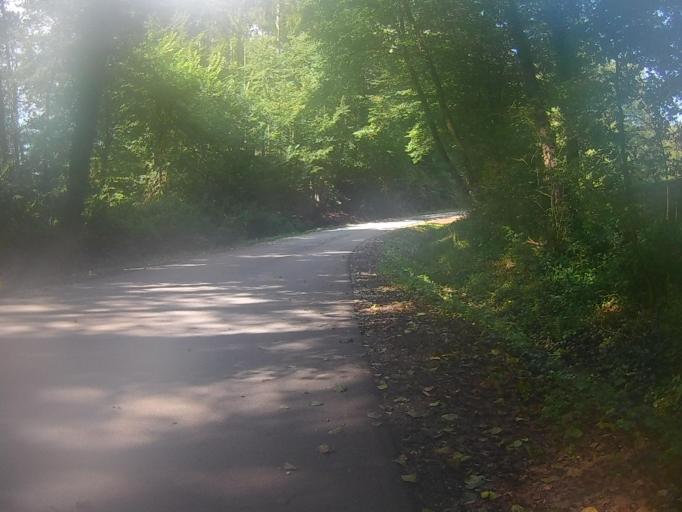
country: SI
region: Starse
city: Starse
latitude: 46.4854
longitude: 15.8149
